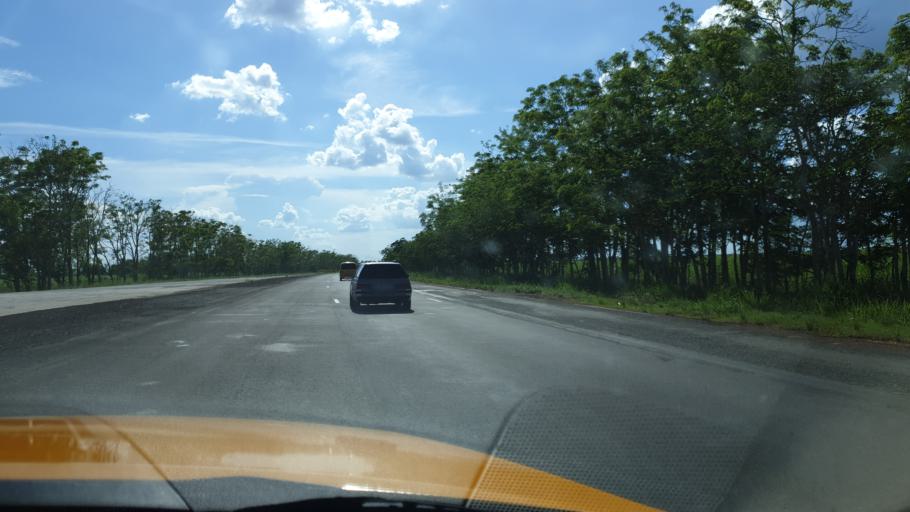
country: CU
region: Cienfuegos
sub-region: Municipio de Aguada de Pasajeros
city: Aguada de Pasajeros
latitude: 22.4022
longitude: -80.8549
